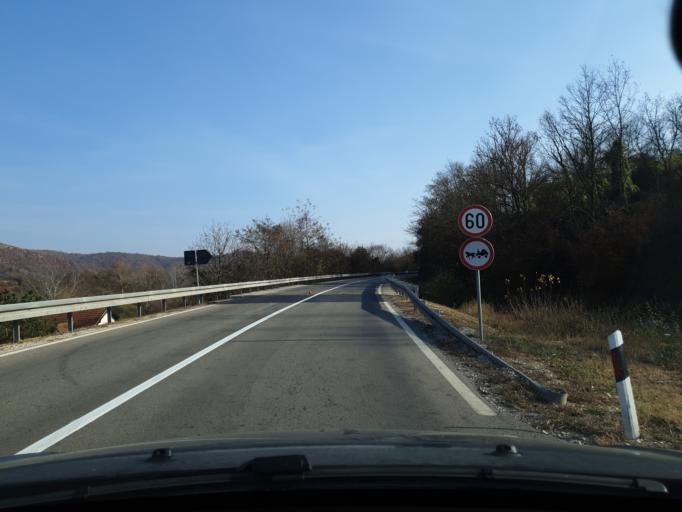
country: RS
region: Central Serbia
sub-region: Zajecarski Okrug
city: Zajecar
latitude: 43.9290
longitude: 22.1691
